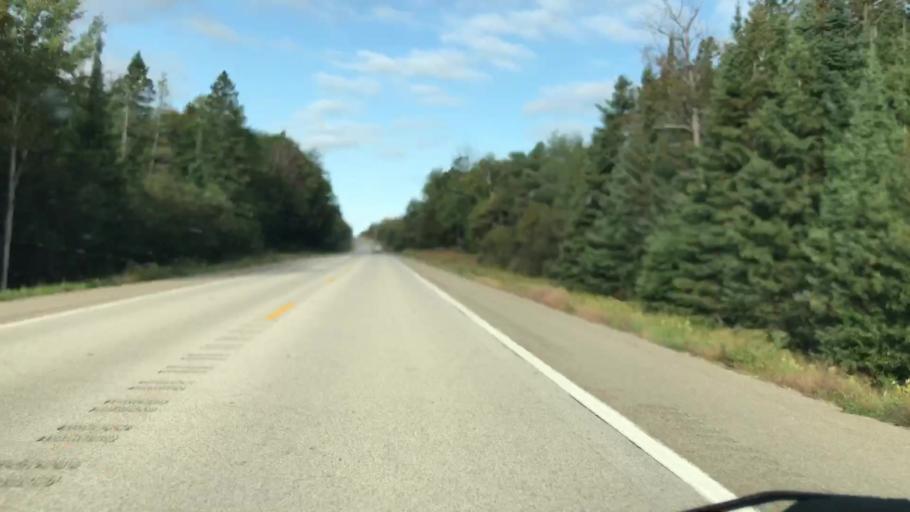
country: US
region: Michigan
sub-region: Luce County
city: Newberry
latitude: 46.3321
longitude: -85.0913
